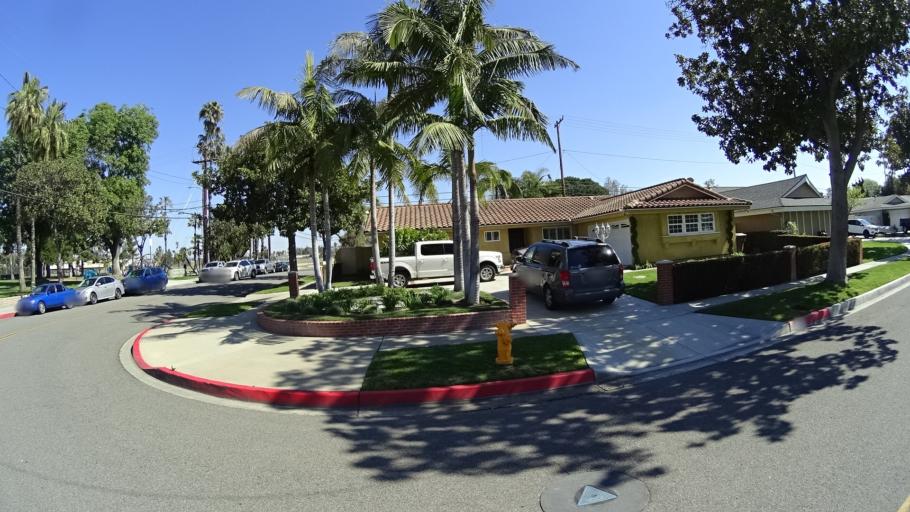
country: US
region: California
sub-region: Orange County
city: Anaheim
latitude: 33.8141
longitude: -117.9375
